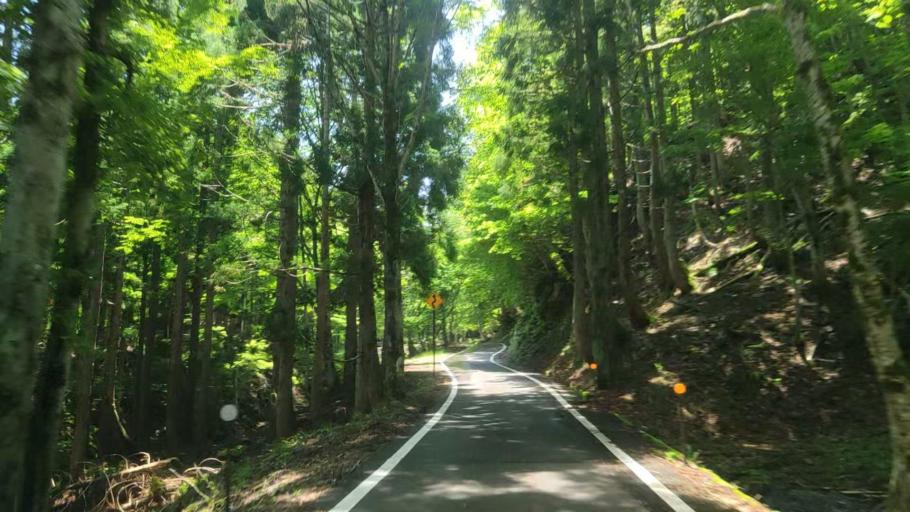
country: JP
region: Tottori
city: Tottori
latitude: 35.3756
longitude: 134.4902
